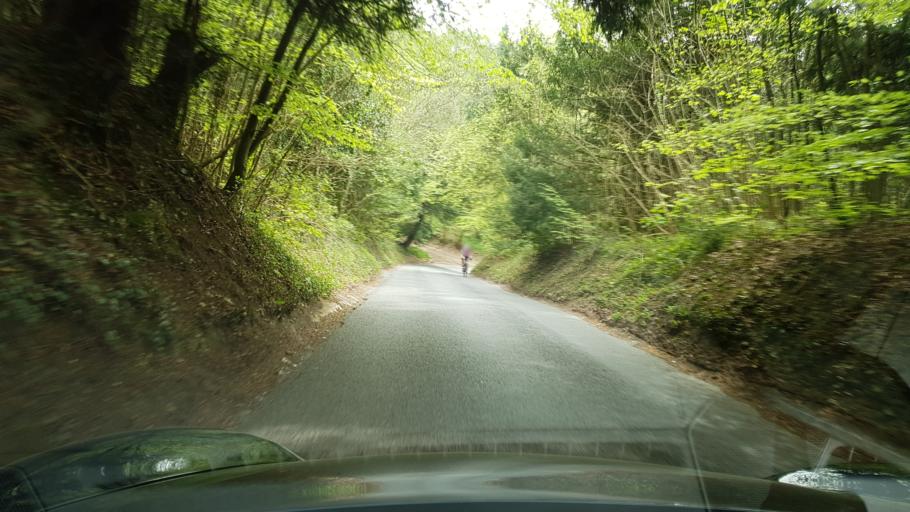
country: GB
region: England
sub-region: Surrey
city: East Horsley
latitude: 51.2317
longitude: -0.4673
